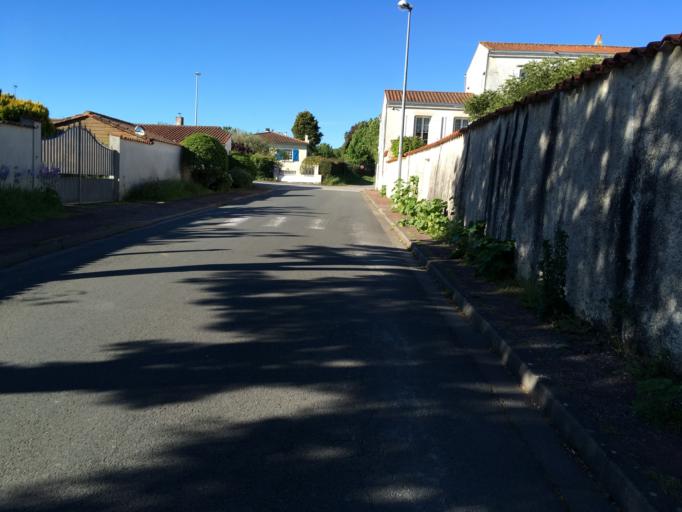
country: FR
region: Poitou-Charentes
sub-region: Departement de la Charente-Maritime
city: Nieul-sur-Mer
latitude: 46.1917
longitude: -1.1853
